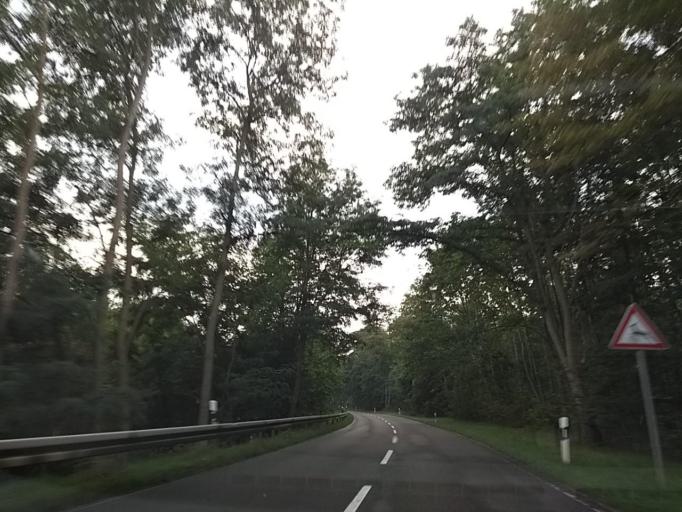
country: DE
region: Saxony-Anhalt
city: Theissen
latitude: 51.1089
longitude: 12.1435
